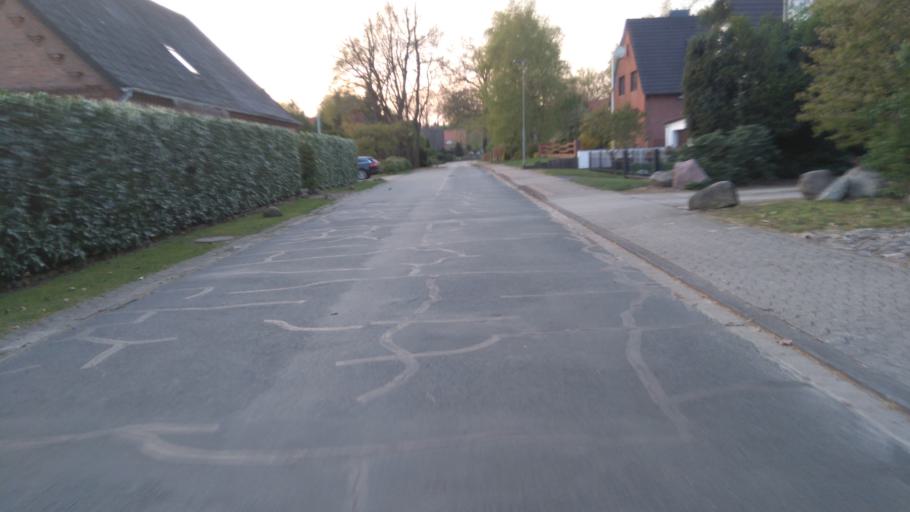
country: DE
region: Lower Saxony
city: Harsefeld
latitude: 53.4825
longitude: 9.5182
